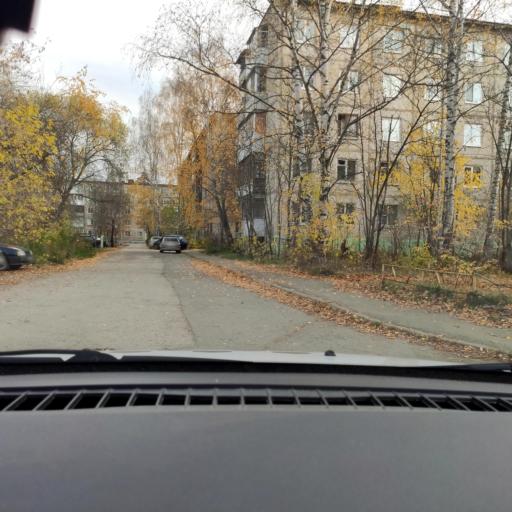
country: RU
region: Perm
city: Kondratovo
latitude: 58.0272
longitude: 56.0073
